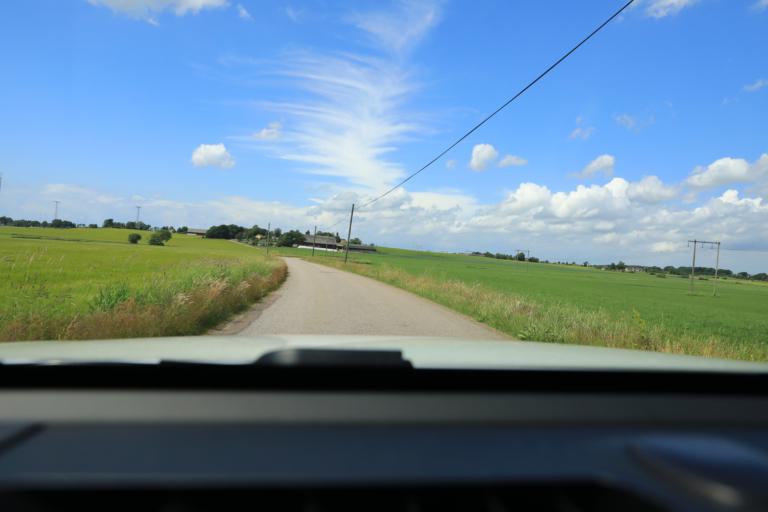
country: SE
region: Halland
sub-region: Varbergs Kommun
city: Tvaaker
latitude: 57.1089
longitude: 12.4416
